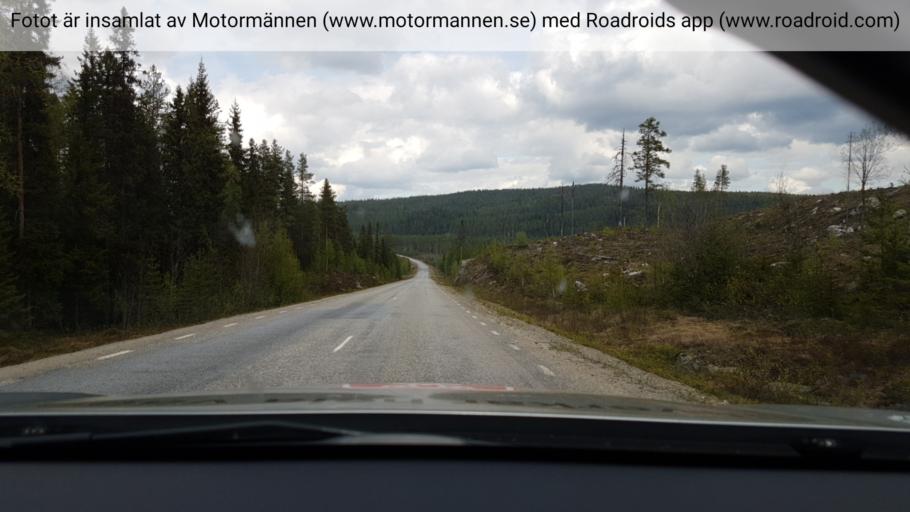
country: SE
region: Vaesternorrland
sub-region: OErnskoeldsviks Kommun
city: Bredbyn
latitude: 63.9238
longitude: 18.4809
